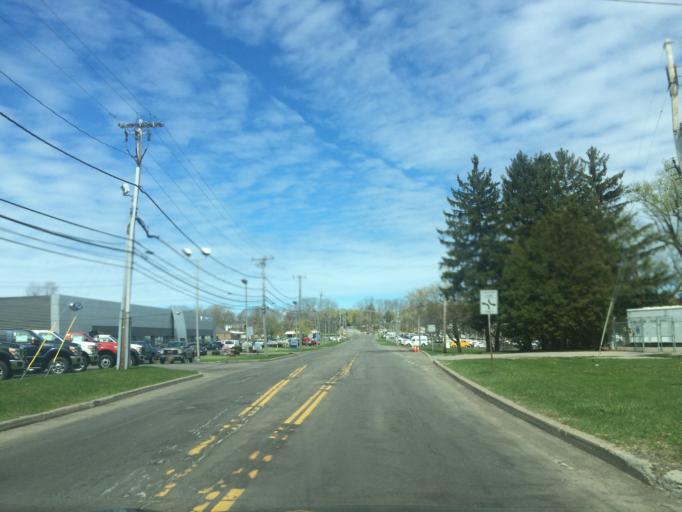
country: US
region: New York
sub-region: Monroe County
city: East Rochester
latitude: 43.0991
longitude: -77.4833
